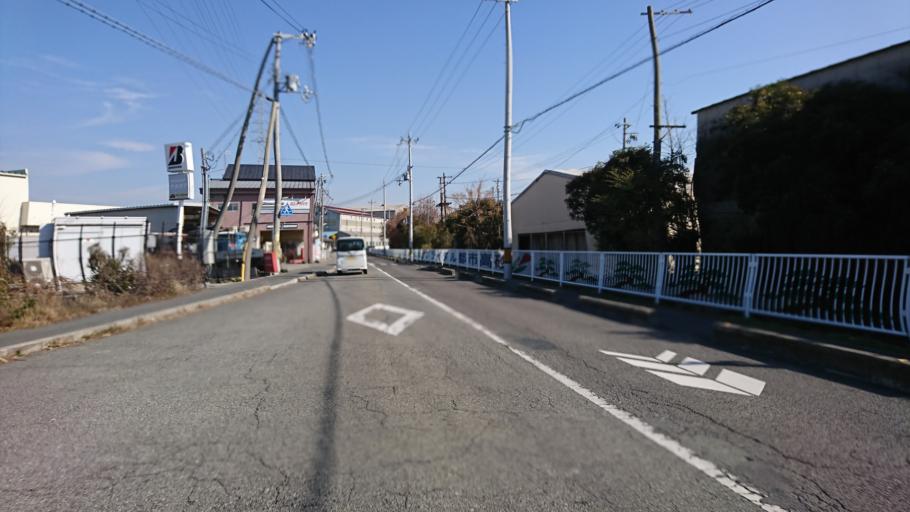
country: JP
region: Hyogo
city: Kakogawacho-honmachi
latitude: 34.7760
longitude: 134.8128
